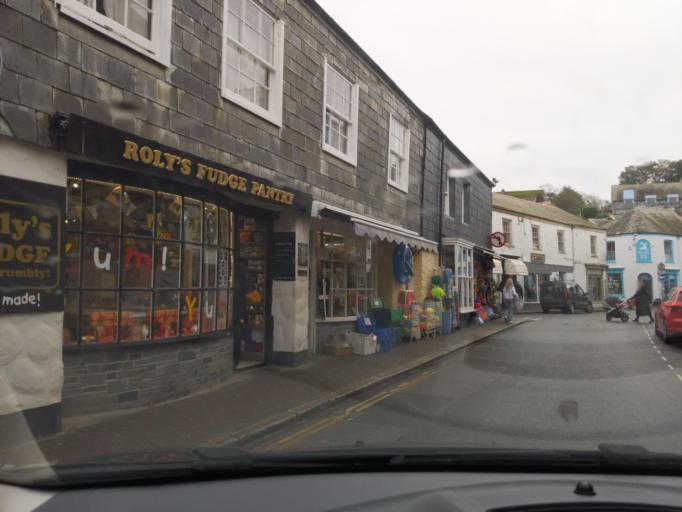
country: GB
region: England
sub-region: Cornwall
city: Padstow
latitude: 50.5414
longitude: -4.9389
